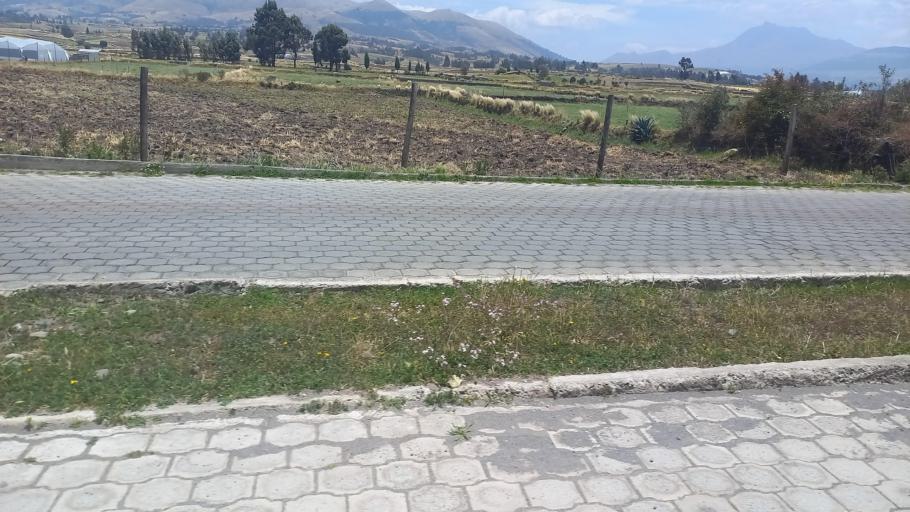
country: EC
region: Pichincha
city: Cayambe
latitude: 0.1462
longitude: -78.0709
